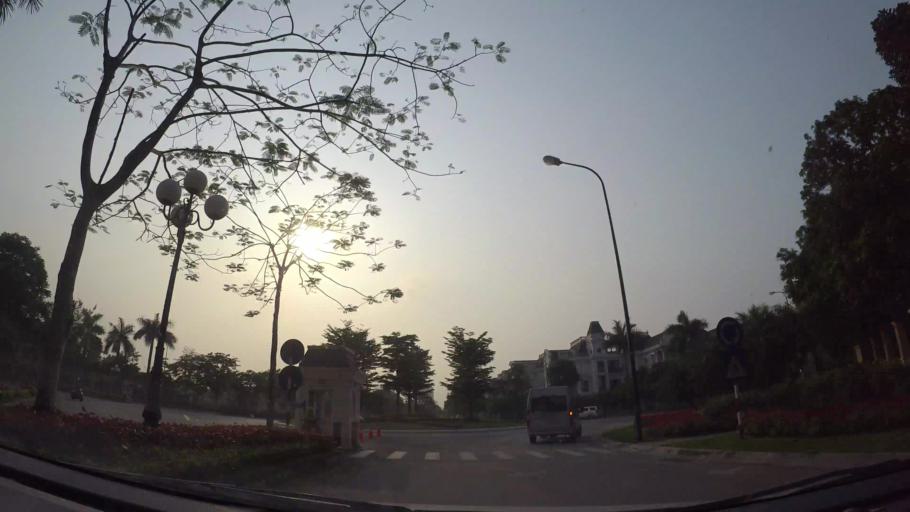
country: VN
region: Ha Noi
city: Tay Ho
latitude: 21.0750
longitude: 105.8010
